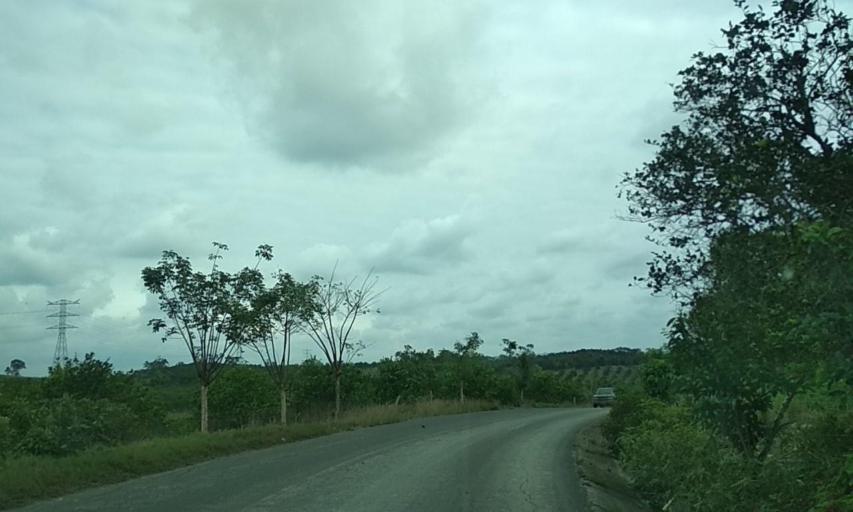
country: MX
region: Veracruz
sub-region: Papantla
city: El Chote
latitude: 20.3501
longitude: -97.3824
